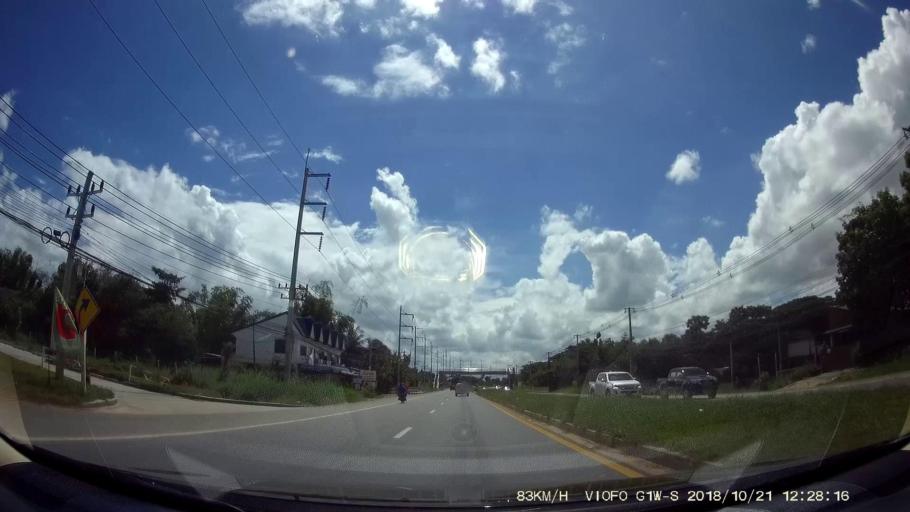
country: TH
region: Nakhon Ratchasima
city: Dan Khun Thot
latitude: 15.1916
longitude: 101.7611
